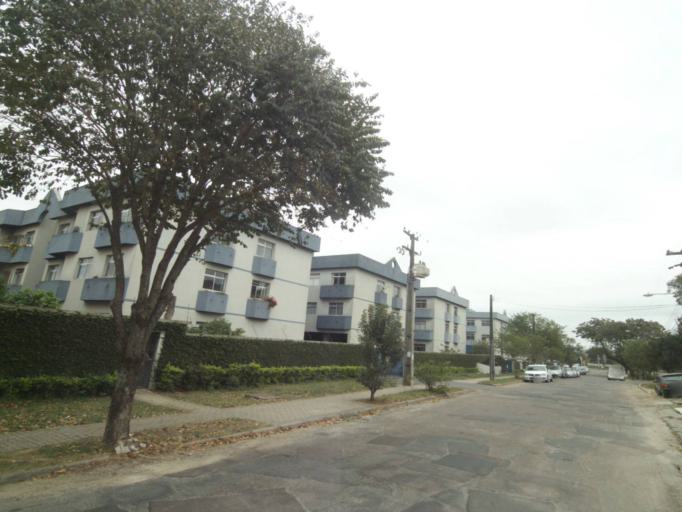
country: BR
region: Parana
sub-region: Pinhais
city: Pinhais
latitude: -25.4757
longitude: -49.2382
